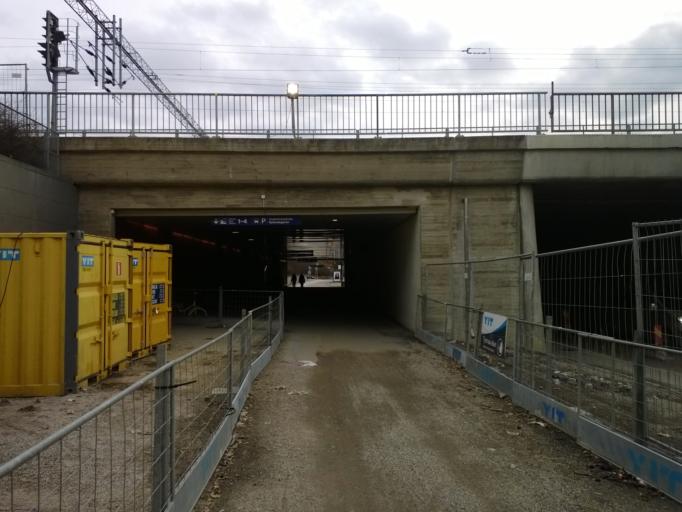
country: FI
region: Paijanne Tavastia
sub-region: Lahti
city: Lahti
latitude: 60.9767
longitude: 25.6592
